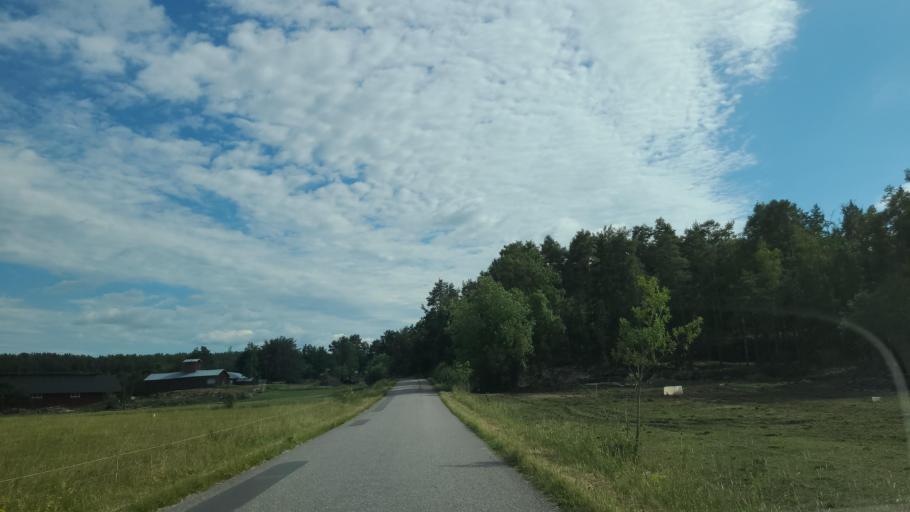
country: FI
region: Varsinais-Suomi
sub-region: Turku
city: Rymaettylae
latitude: 60.2961
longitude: 21.9370
